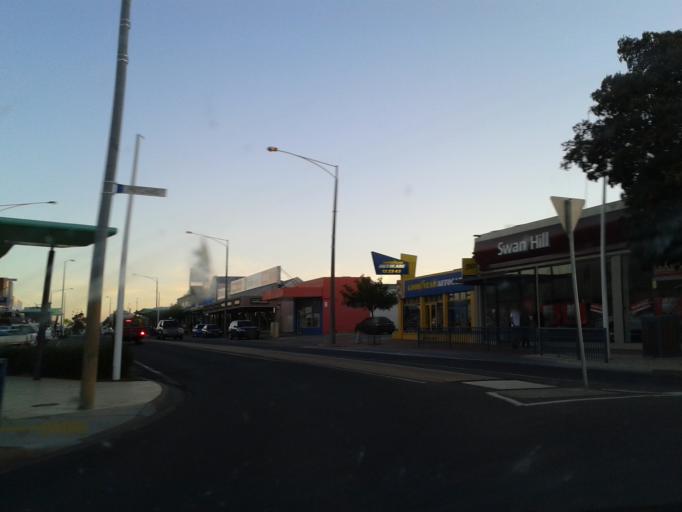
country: AU
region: Victoria
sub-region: Swan Hill
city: Swan Hill
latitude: -35.3364
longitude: 143.5589
